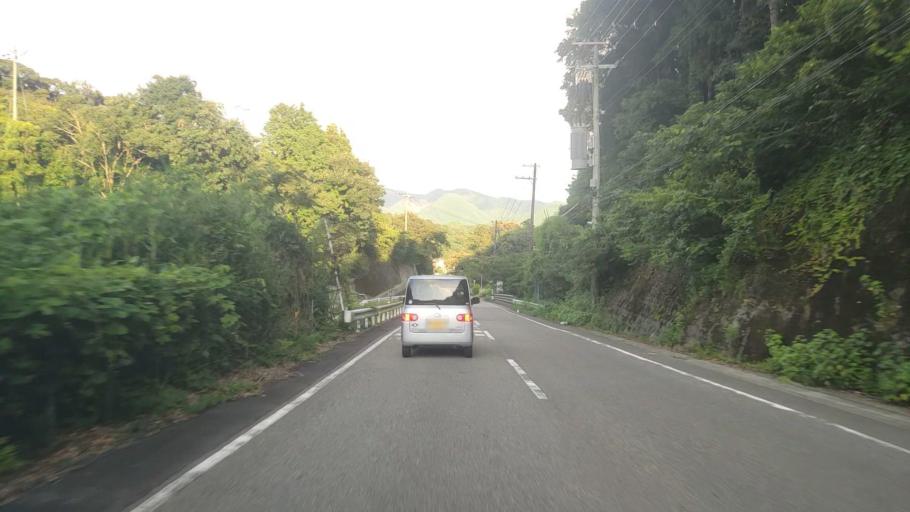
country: JP
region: Wakayama
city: Tanabe
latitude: 33.7274
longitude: 135.4382
